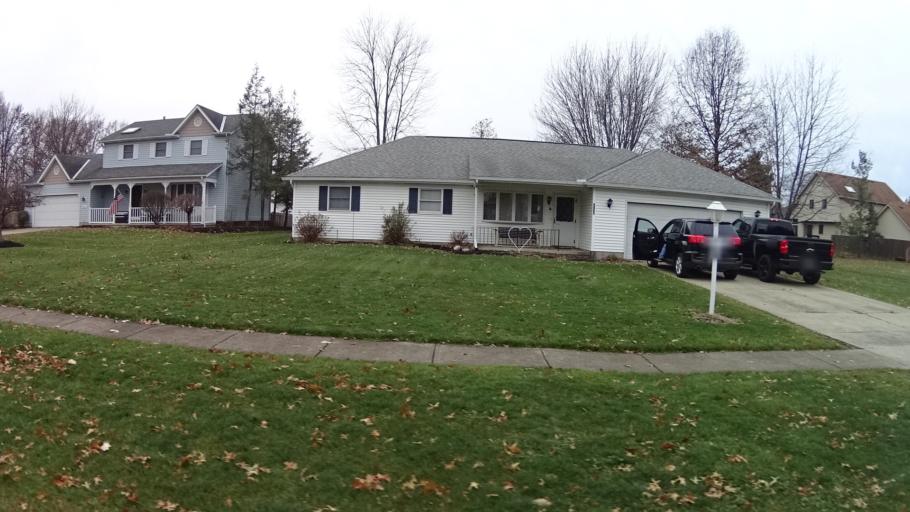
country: US
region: Ohio
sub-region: Lorain County
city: North Ridgeville
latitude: 41.3616
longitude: -81.9960
